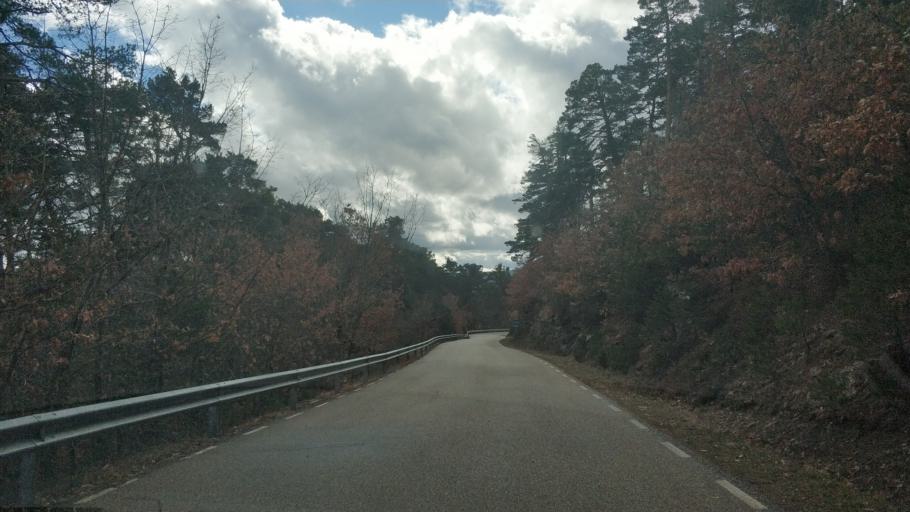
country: ES
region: Castille and Leon
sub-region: Provincia de Burgos
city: Quintanar de la Sierra
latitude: 41.9991
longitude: -3.0164
